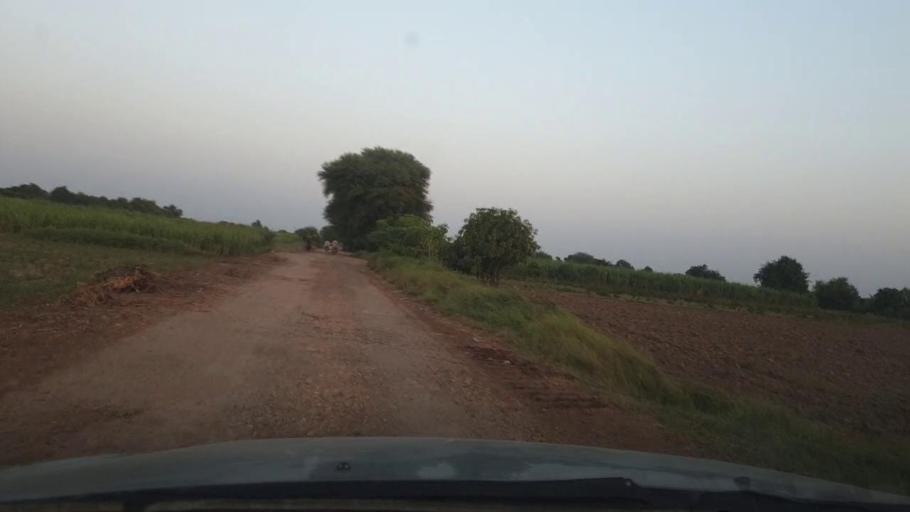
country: PK
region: Sindh
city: Digri
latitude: 25.1113
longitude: 68.9994
